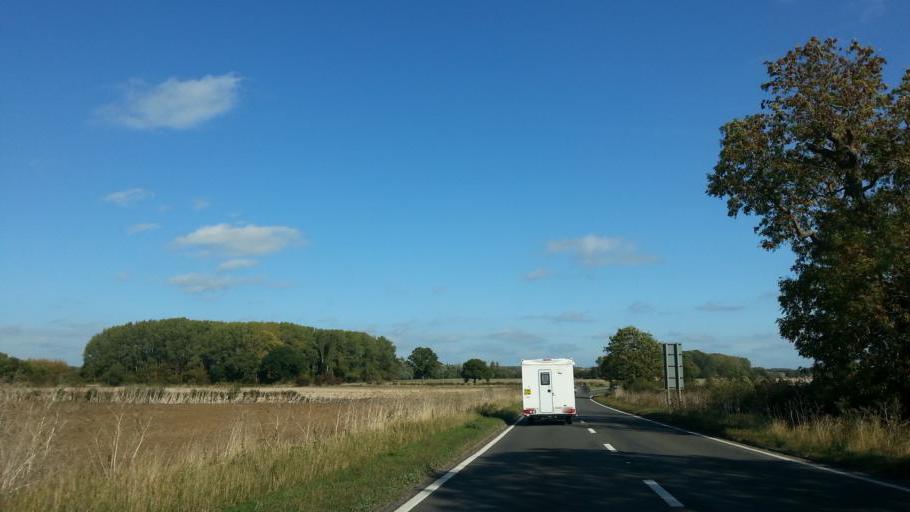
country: GB
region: England
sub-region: Northamptonshire
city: Thrapston
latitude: 52.4125
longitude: -0.5078
